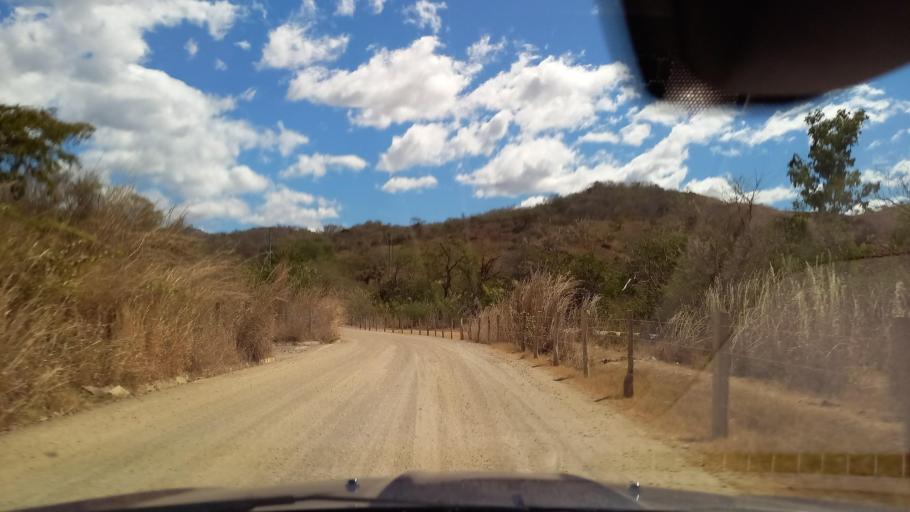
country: SV
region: Santa Ana
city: Metapan
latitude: 14.3594
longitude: -89.4668
